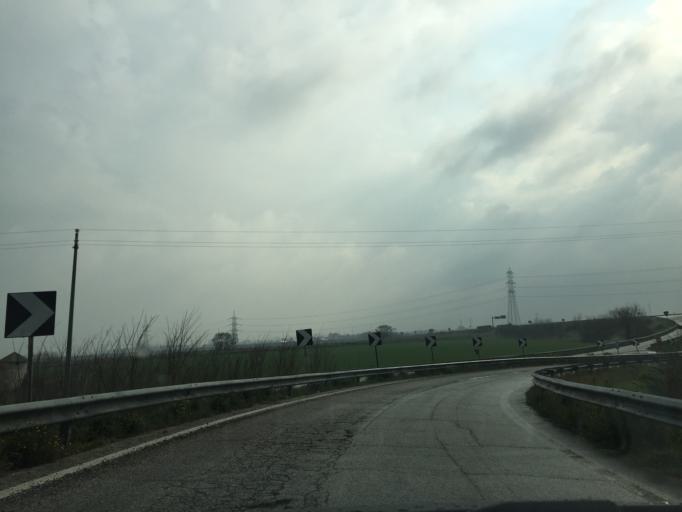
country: IT
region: Apulia
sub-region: Provincia di Foggia
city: Foggia
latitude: 41.4988
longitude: 15.5178
